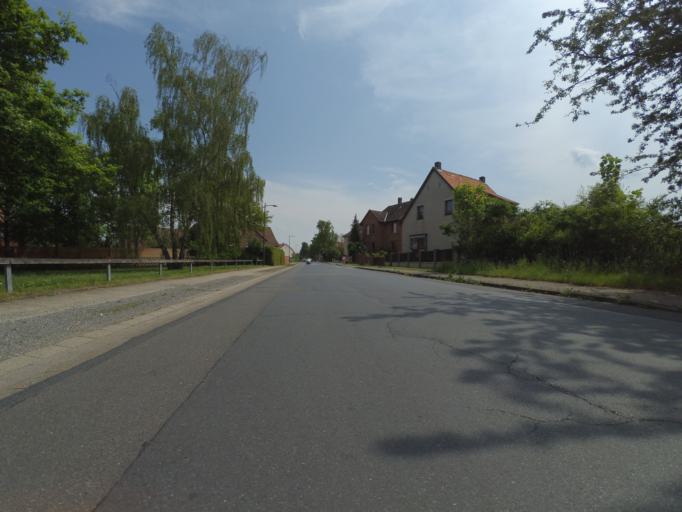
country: DE
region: Lower Saxony
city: Dollbergen
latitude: 52.3496
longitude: 10.1855
